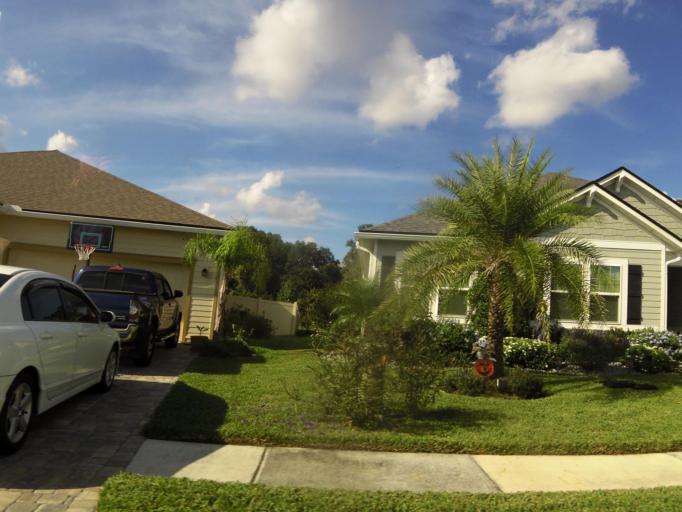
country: US
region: Florida
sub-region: Saint Johns County
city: Saint Augustine
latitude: 29.9291
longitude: -81.4930
